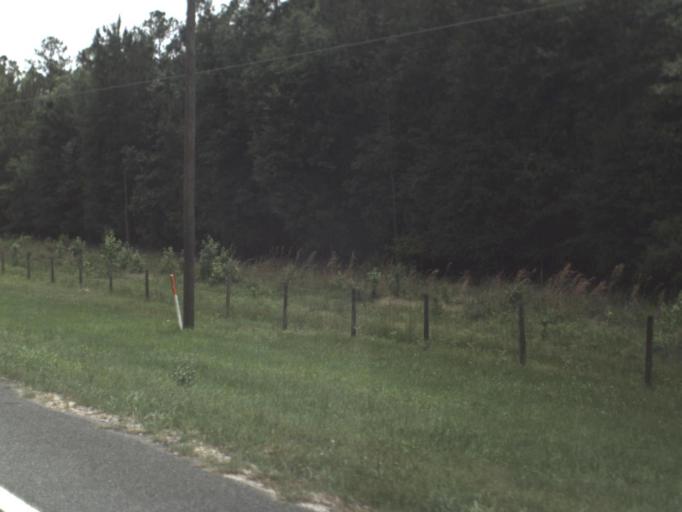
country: US
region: Florida
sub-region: Clay County
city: Asbury Lake
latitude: 29.9090
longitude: -81.8974
